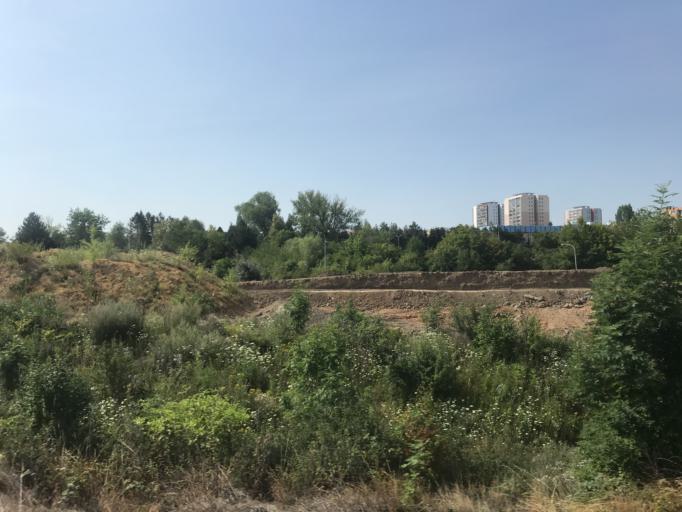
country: CZ
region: Praha
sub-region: Praha 14
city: Hostavice
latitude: 50.0548
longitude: 14.5494
